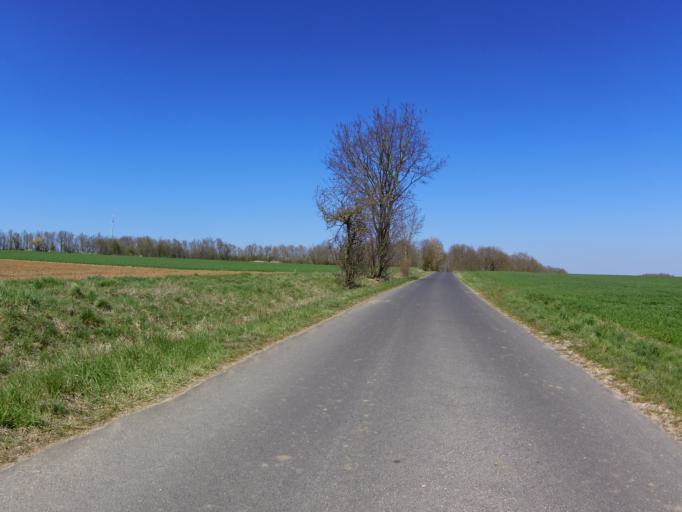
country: DE
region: Bavaria
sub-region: Regierungsbezirk Unterfranken
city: Biebelried
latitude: 49.7715
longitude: 10.0804
